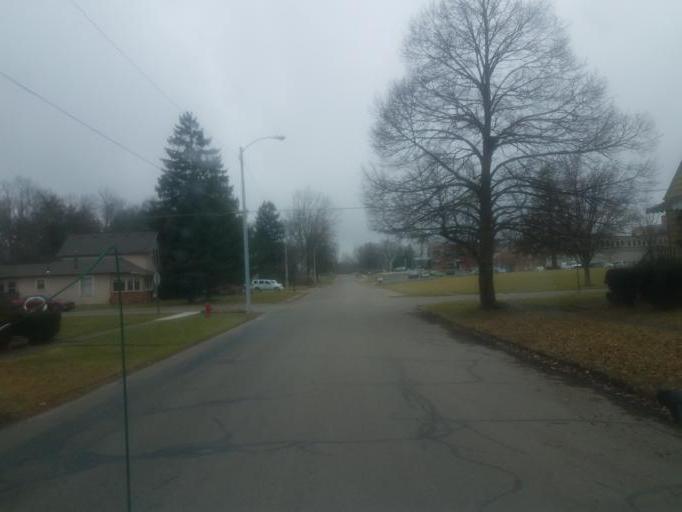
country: US
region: Ohio
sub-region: Crawford County
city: Galion
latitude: 40.7301
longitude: -82.7998
